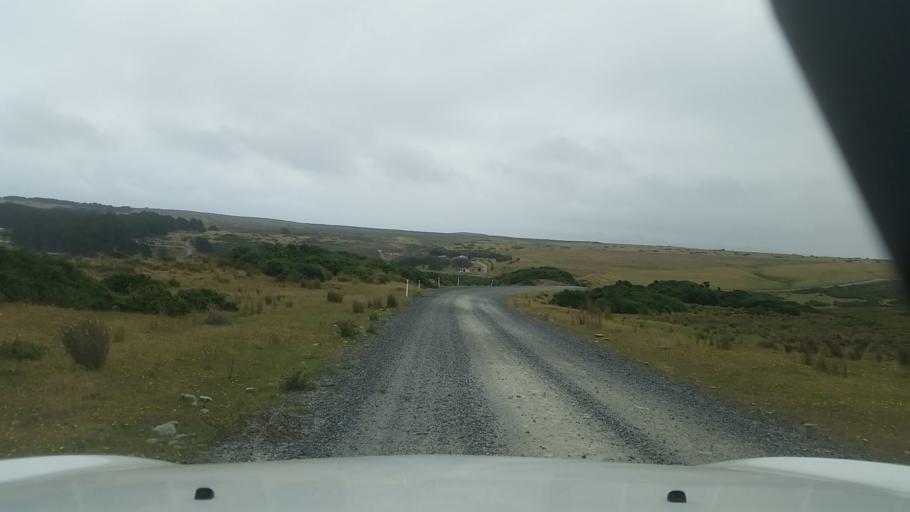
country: NZ
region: Chatham Islands
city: Waitangi
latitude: -43.8065
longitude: -176.7028
